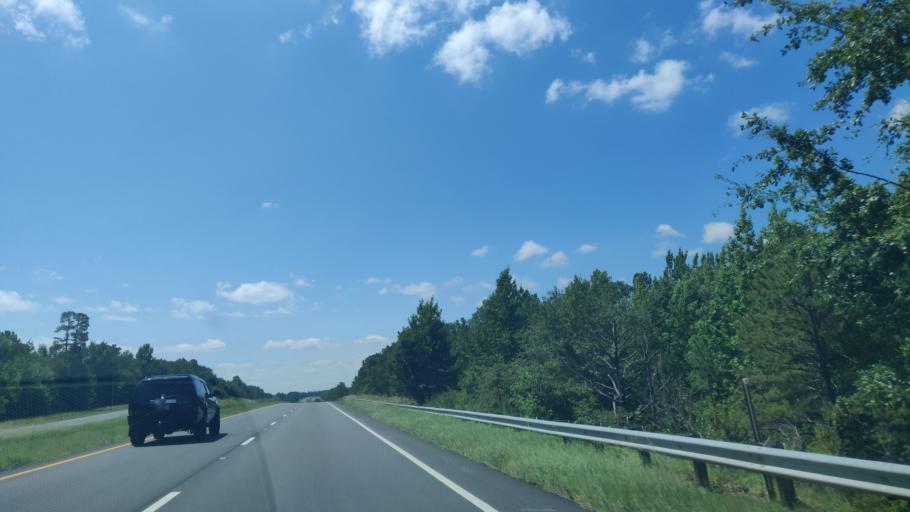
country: US
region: Georgia
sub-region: Chattahoochee County
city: Cusseta
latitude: 32.2156
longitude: -84.7090
